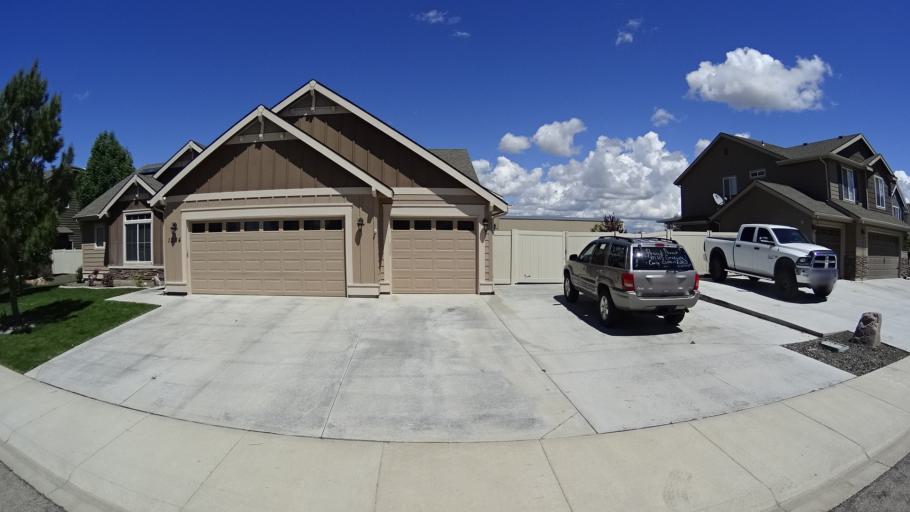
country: US
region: Idaho
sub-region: Ada County
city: Kuna
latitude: 43.5132
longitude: -116.4299
